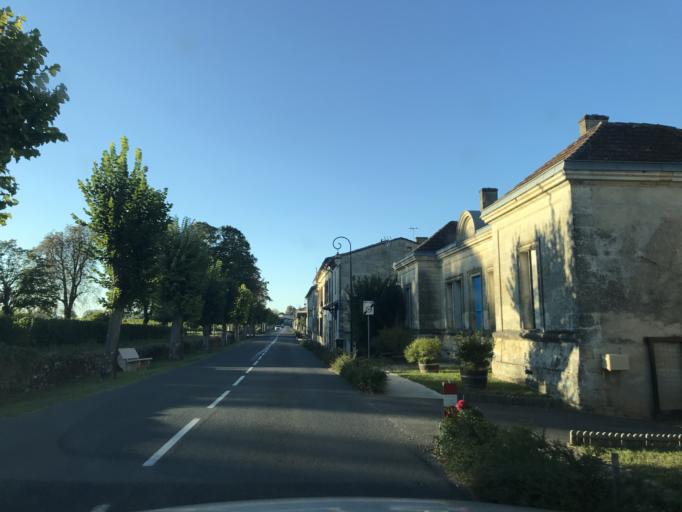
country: FR
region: Aquitaine
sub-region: Departement de la Gironde
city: Lussac
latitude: 44.9251
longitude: -0.0746
